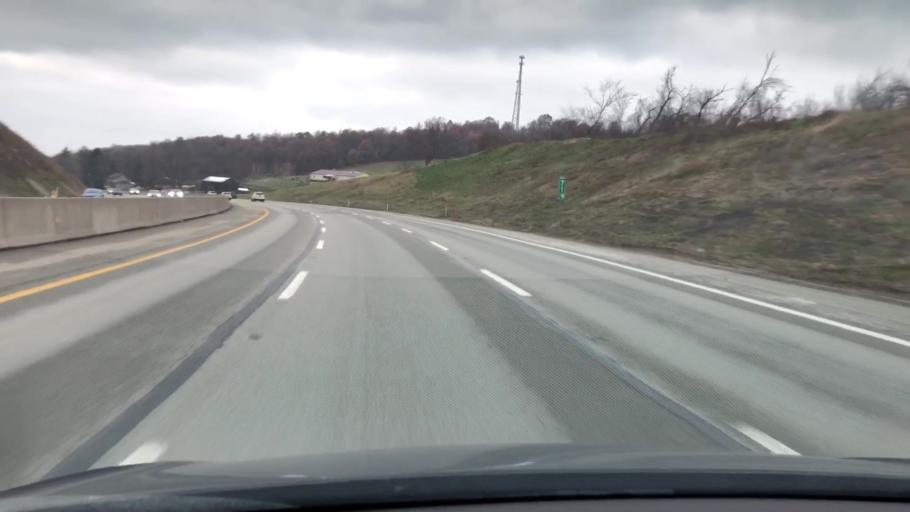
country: US
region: Pennsylvania
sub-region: Westmoreland County
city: New Stanton
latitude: 40.2589
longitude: -79.6430
